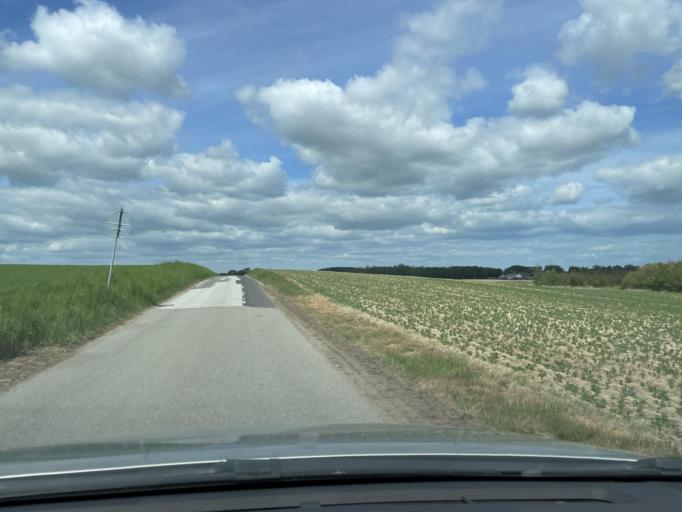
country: DK
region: Central Jutland
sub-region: Odder Kommune
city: Odder
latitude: 55.9033
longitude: 10.1194
